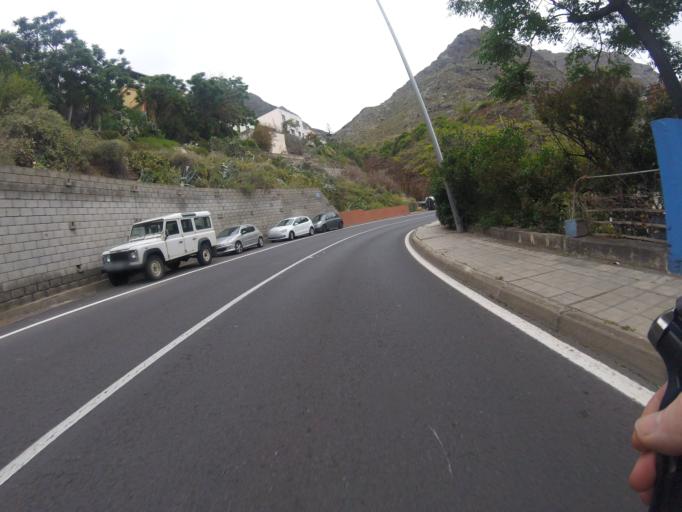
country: ES
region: Canary Islands
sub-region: Provincia de Santa Cruz de Tenerife
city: Tegueste
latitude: 28.5625
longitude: -16.3314
